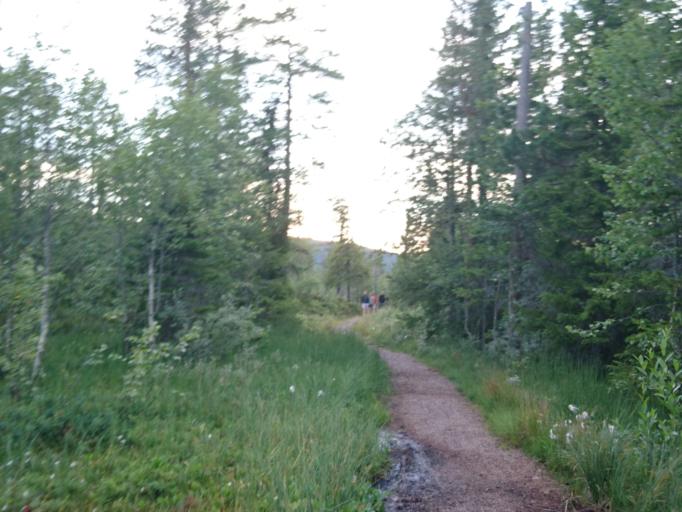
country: SE
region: Dalarna
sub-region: Malung-Saelens kommun
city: Malung
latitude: 61.1726
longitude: 13.1813
